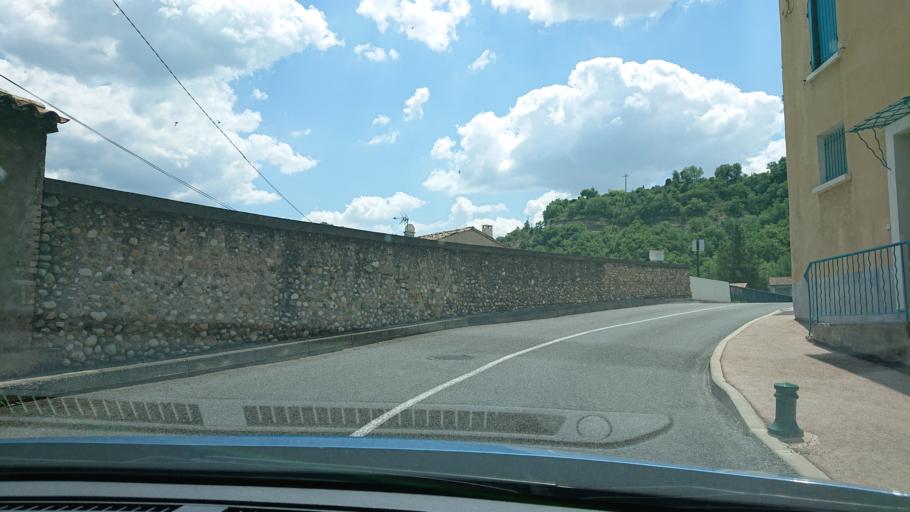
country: FR
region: Provence-Alpes-Cote d'Azur
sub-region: Departement des Alpes-de-Haute-Provence
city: Malijai
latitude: 44.0443
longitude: 6.0307
